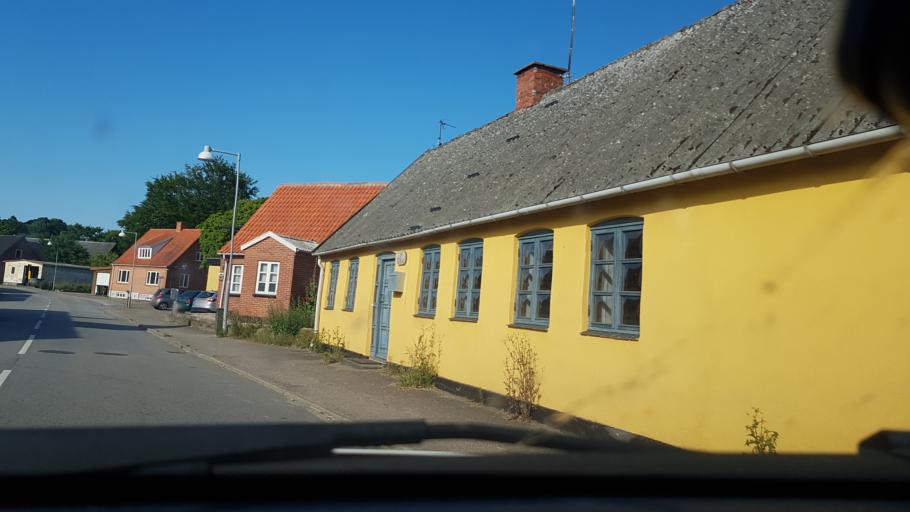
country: DK
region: Zealand
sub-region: Odsherred Kommune
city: Hojby
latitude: 55.8805
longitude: 11.6071
